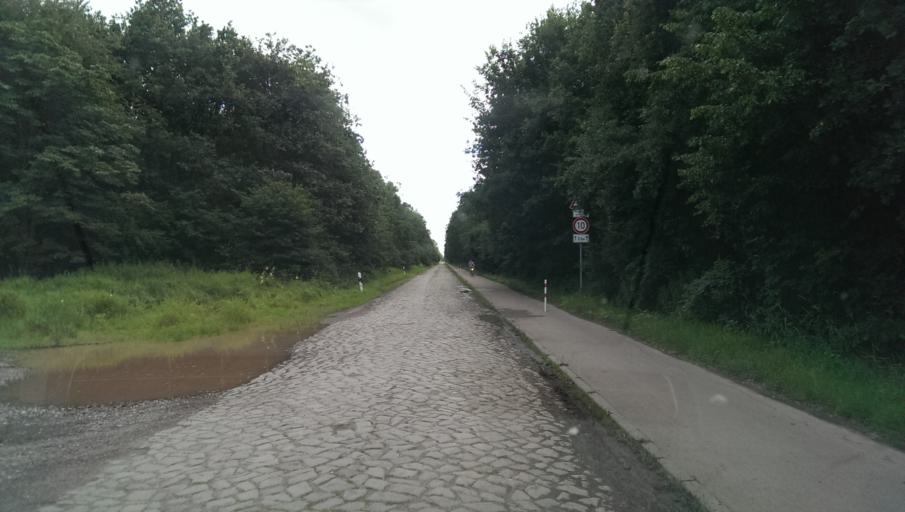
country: DE
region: Saxony-Anhalt
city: Coswig
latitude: 51.8651
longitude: 12.4406
